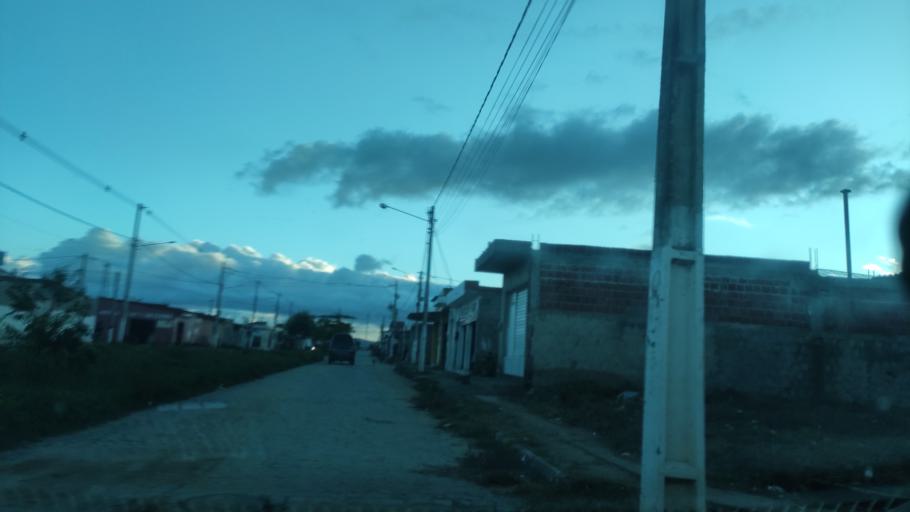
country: BR
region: Alagoas
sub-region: Uniao Dos Palmares
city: Uniao dos Palmares
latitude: -9.1479
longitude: -36.0046
